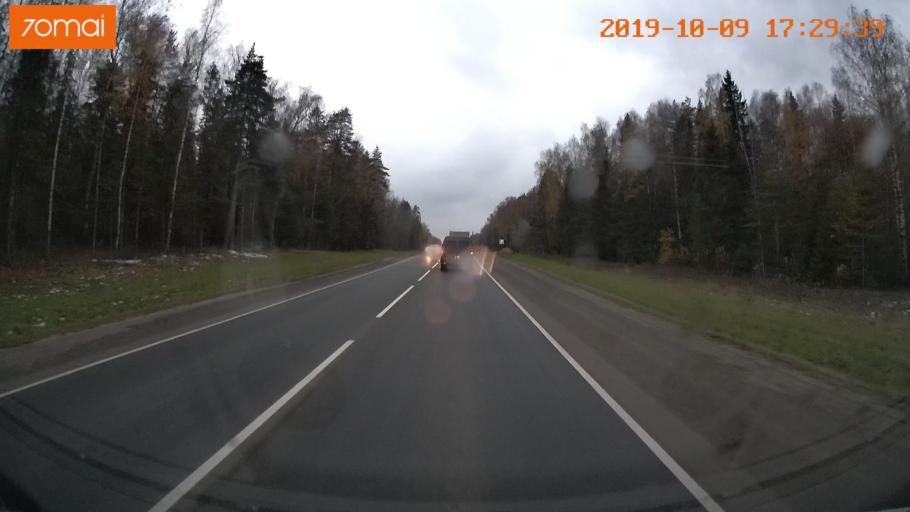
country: RU
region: Ivanovo
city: Bogorodskoye
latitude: 57.1486
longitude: 41.0576
